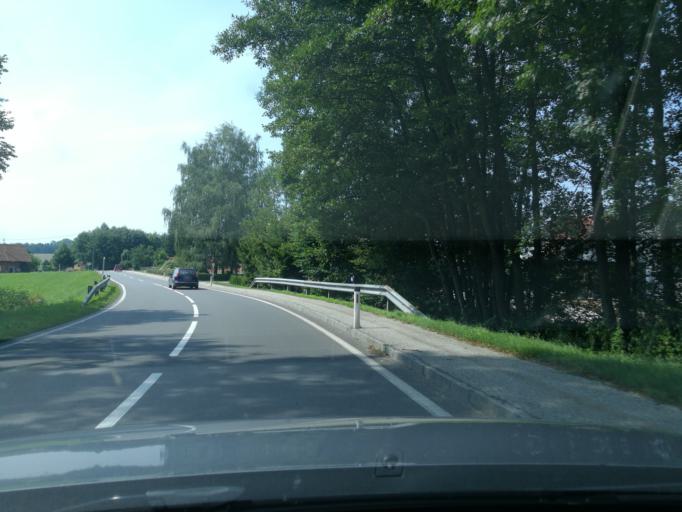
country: AT
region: Upper Austria
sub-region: Politischer Bezirk Grieskirchen
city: Grieskirchen
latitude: 48.3490
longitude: 13.7516
